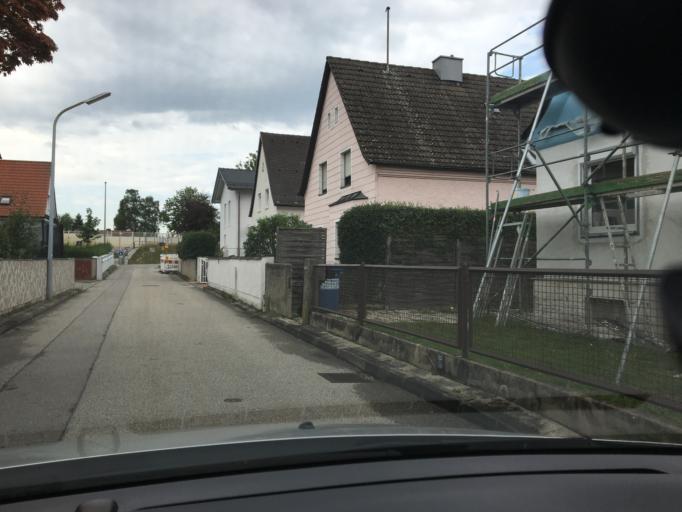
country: DE
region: Bavaria
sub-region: Upper Bavaria
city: Muehldorf
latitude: 48.2466
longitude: 12.5348
